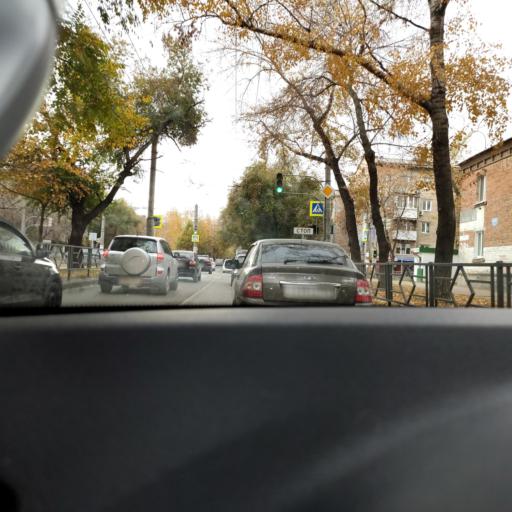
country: RU
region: Samara
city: Samara
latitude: 53.2166
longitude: 50.2371
